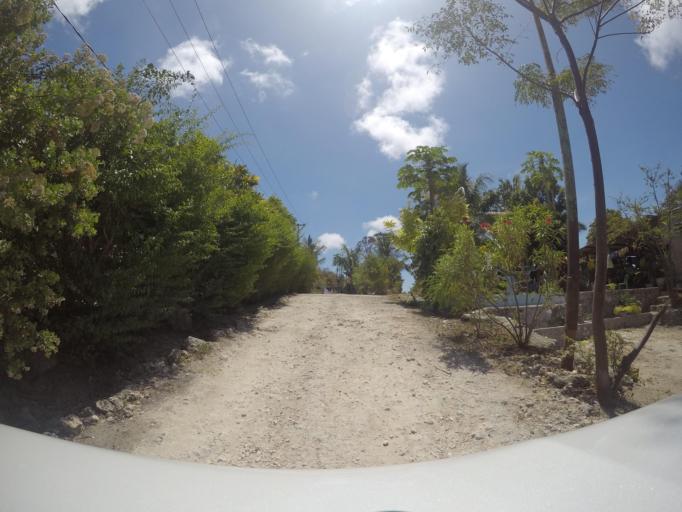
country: TL
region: Baucau
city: Baucau
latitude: -8.4489
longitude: 126.4387
